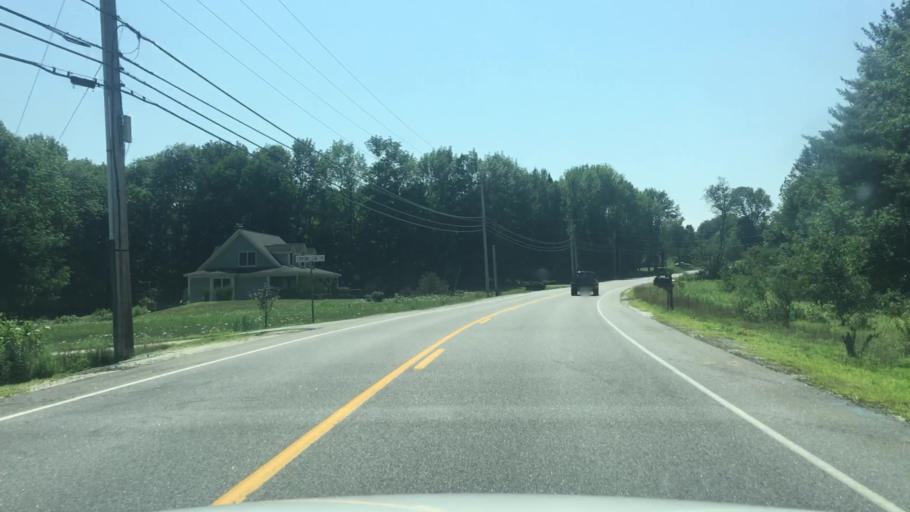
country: US
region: Maine
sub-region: Cumberland County
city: Cumberland Center
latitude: 43.8167
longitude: -70.2904
